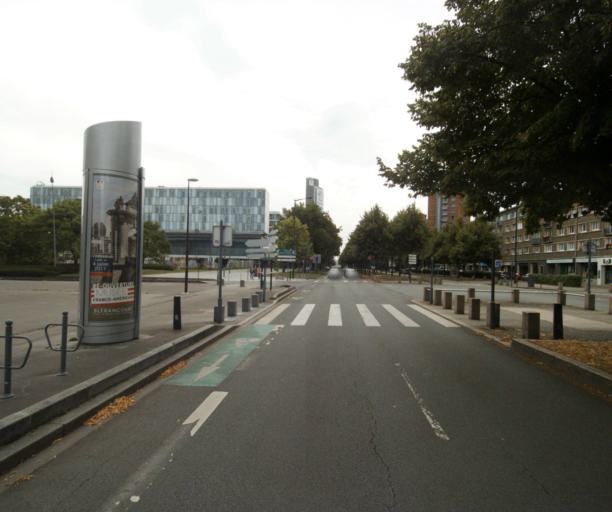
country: FR
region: Nord-Pas-de-Calais
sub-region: Departement du Nord
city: La Madeleine
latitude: 50.6315
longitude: 3.0771
